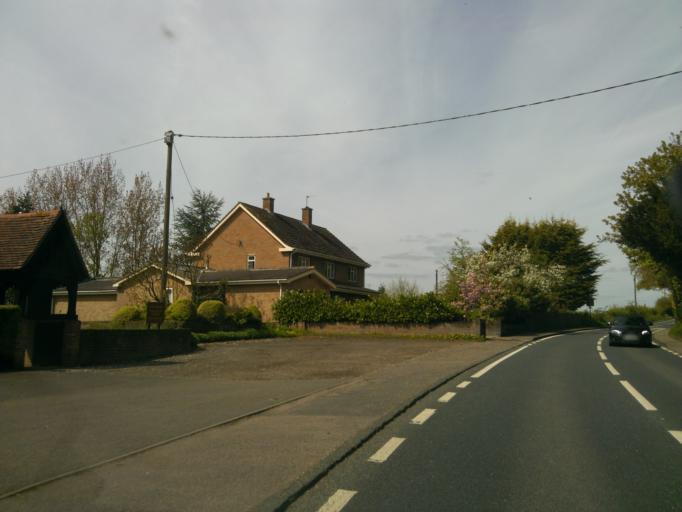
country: GB
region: England
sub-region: Essex
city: Earls Colne
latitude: 51.9242
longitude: 0.7470
